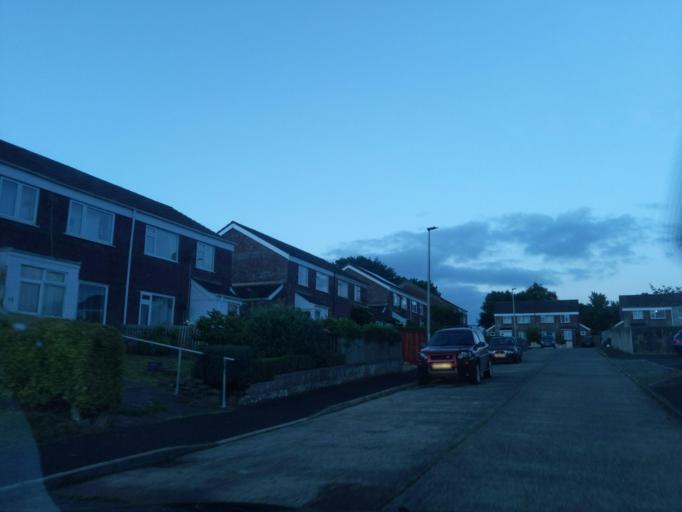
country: GB
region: England
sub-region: Devon
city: Great Torrington
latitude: 50.9585
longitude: -4.1319
